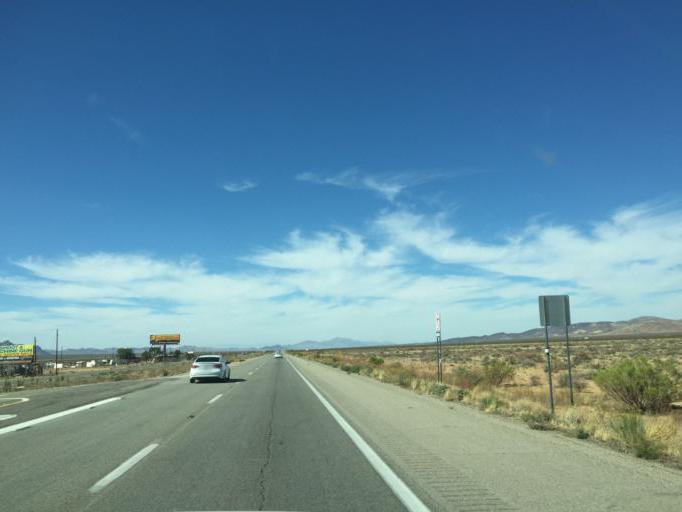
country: US
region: Arizona
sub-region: Mohave County
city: Dolan Springs
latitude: 35.5579
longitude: -114.3717
